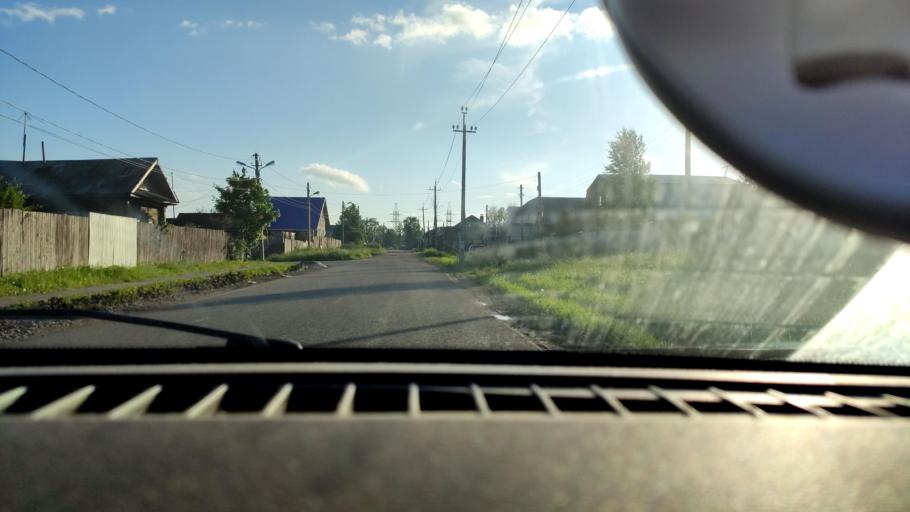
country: RU
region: Perm
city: Novyye Lyady
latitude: 58.0544
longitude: 56.6009
